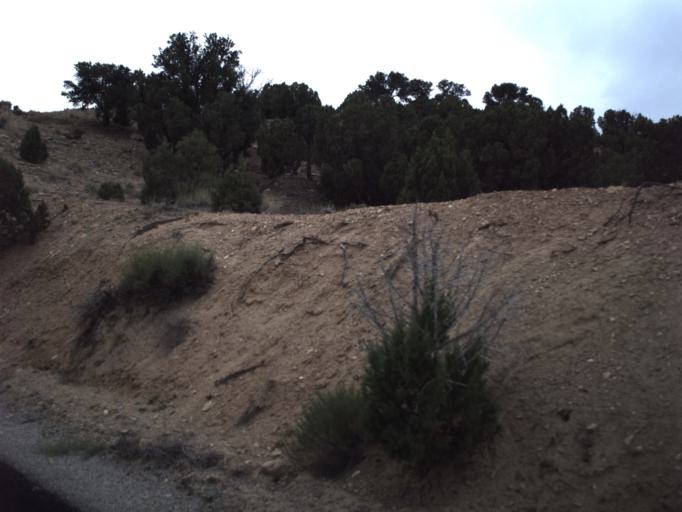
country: US
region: Utah
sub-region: Carbon County
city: East Carbon City
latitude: 39.4863
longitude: -110.4039
